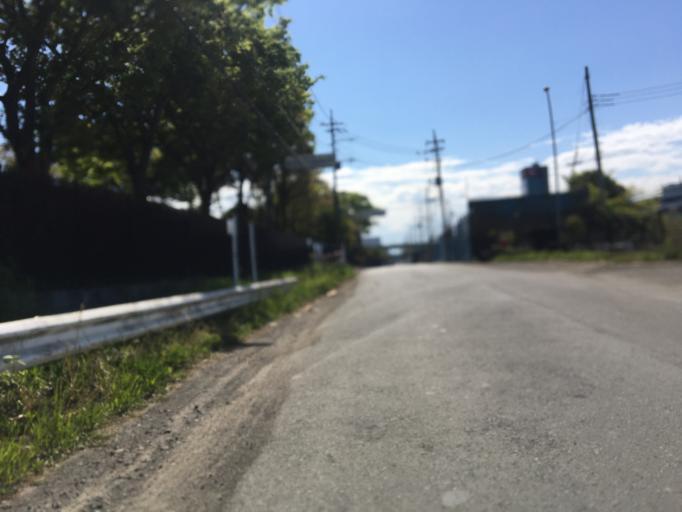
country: JP
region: Saitama
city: Asaka
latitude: 35.8062
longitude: 139.6154
